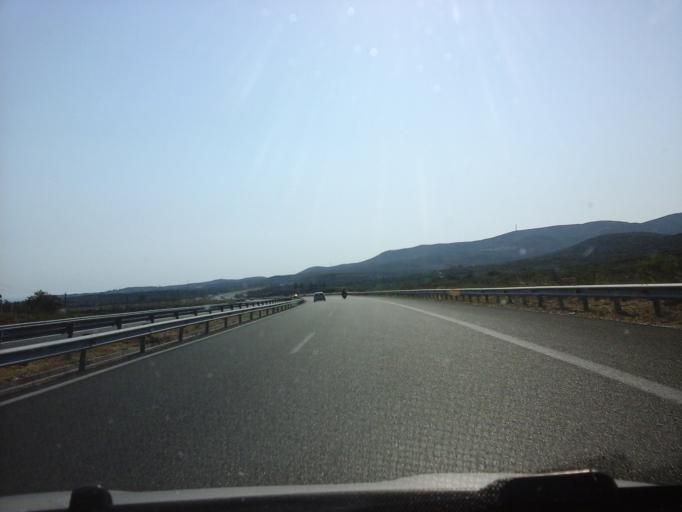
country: GR
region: East Macedonia and Thrace
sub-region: Nomos Evrou
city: Alexandroupoli
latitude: 40.8712
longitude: 25.7913
